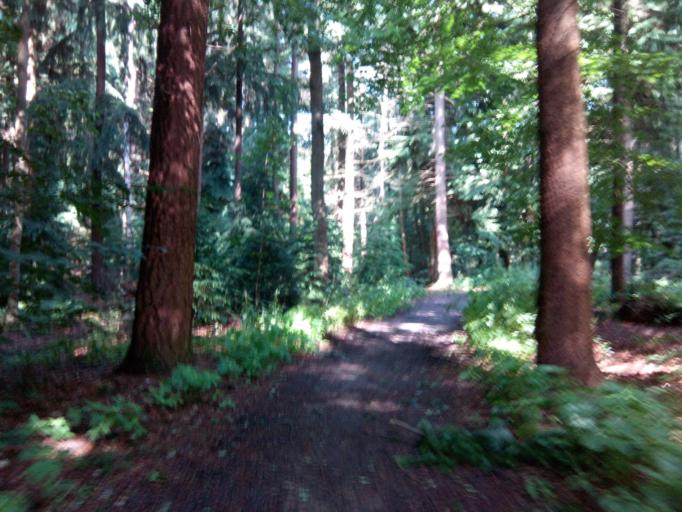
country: NL
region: Utrecht
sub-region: Gemeente Utrechtse Heuvelrug
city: Doorn
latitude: 52.0417
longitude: 5.3226
